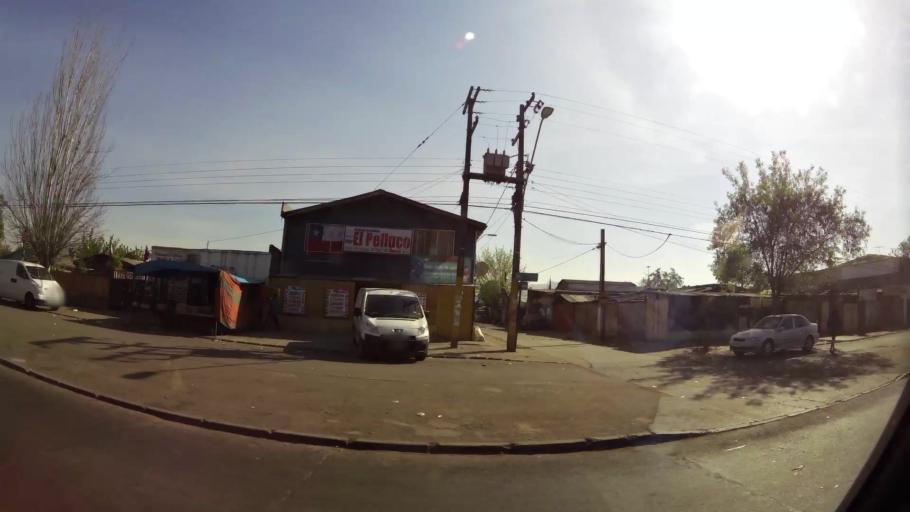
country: CL
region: Santiago Metropolitan
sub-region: Provincia de Santiago
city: Lo Prado
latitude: -33.4167
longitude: -70.7518
